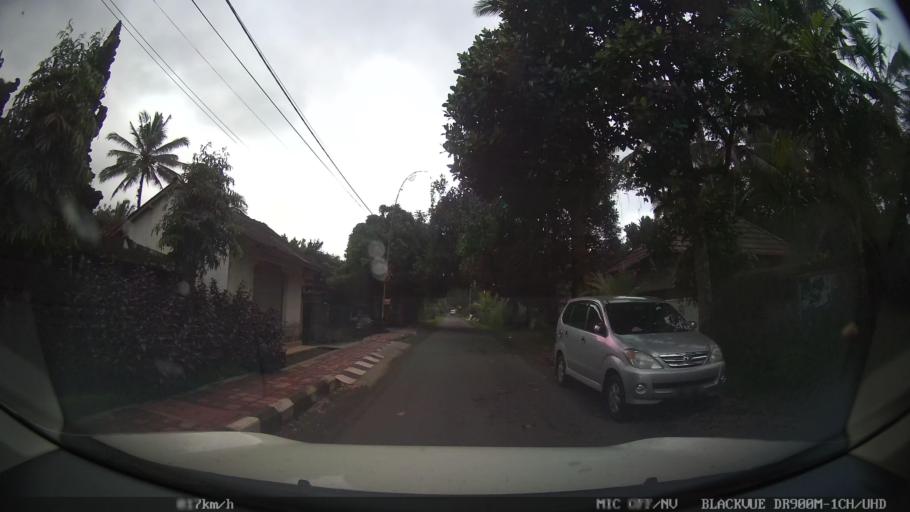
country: ID
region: Bali
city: Banjar Wangsian
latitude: -8.4323
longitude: 115.4255
